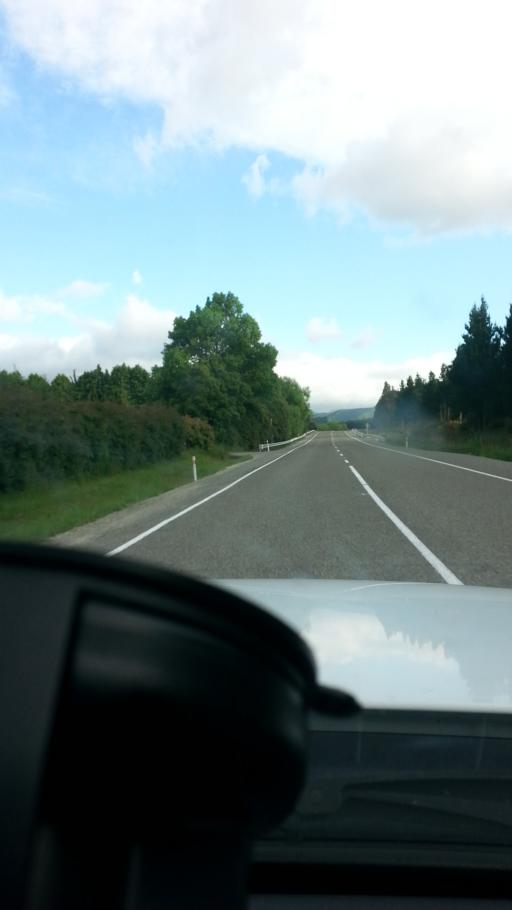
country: NZ
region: Wellington
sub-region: Masterton District
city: Masterton
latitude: -40.8092
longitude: 175.6204
